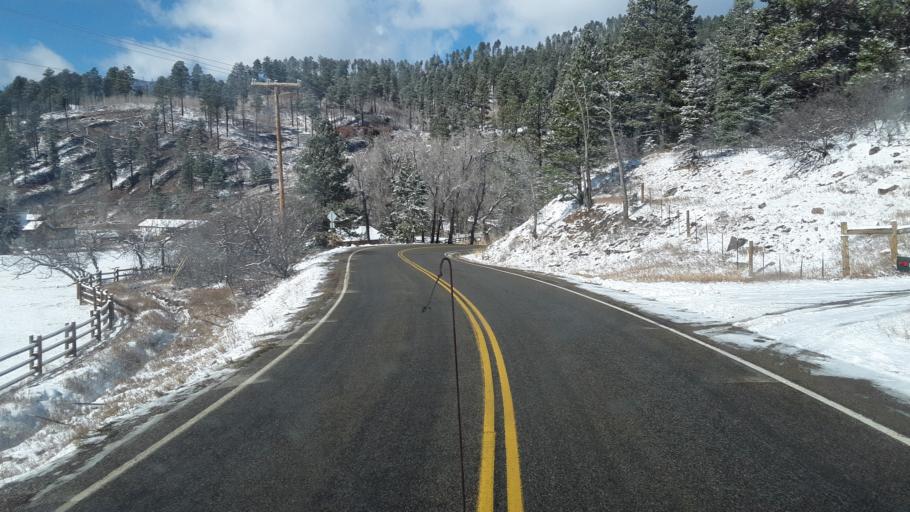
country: US
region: Colorado
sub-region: La Plata County
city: Bayfield
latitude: 37.3591
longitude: -107.6696
